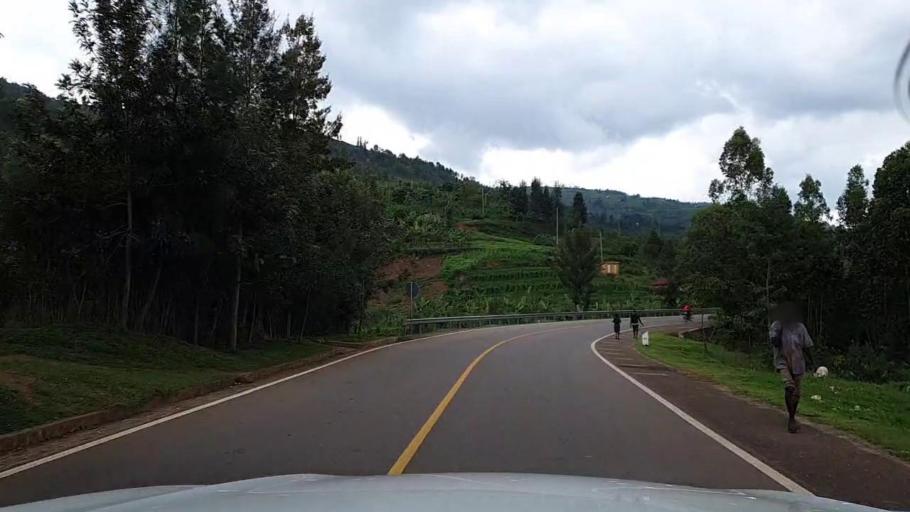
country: RW
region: Northern Province
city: Byumba
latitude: -1.6771
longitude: 30.0982
